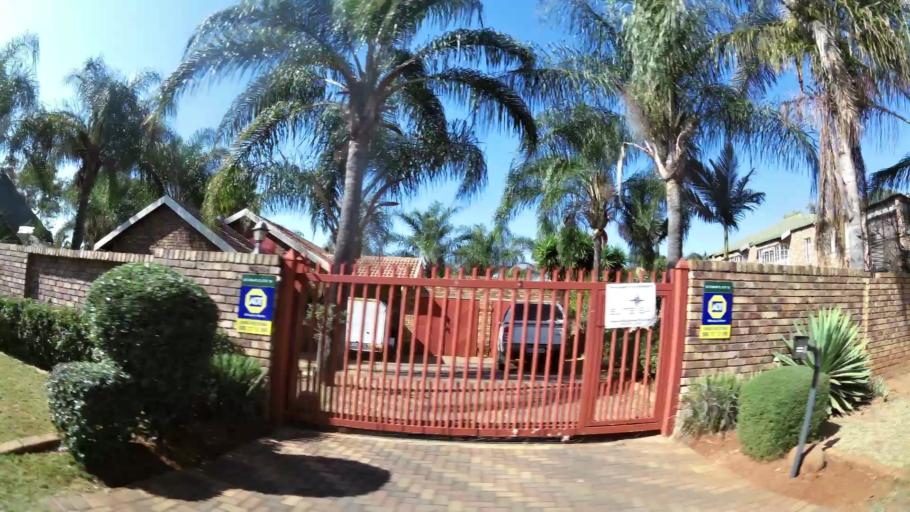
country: ZA
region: Gauteng
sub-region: City of Tshwane Metropolitan Municipality
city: Pretoria
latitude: -25.6588
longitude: 28.2587
